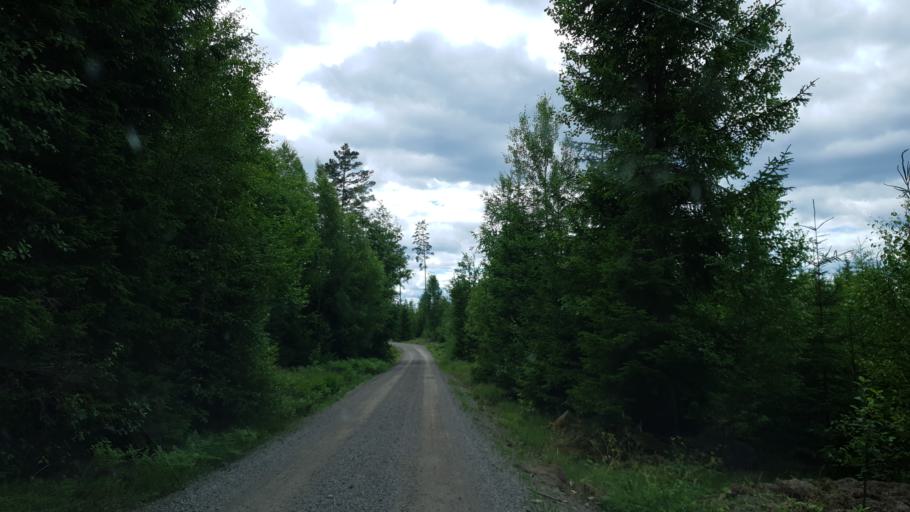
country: SE
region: Kalmar
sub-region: Hultsfreds Kommun
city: Virserum
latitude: 57.0910
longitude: 15.6229
